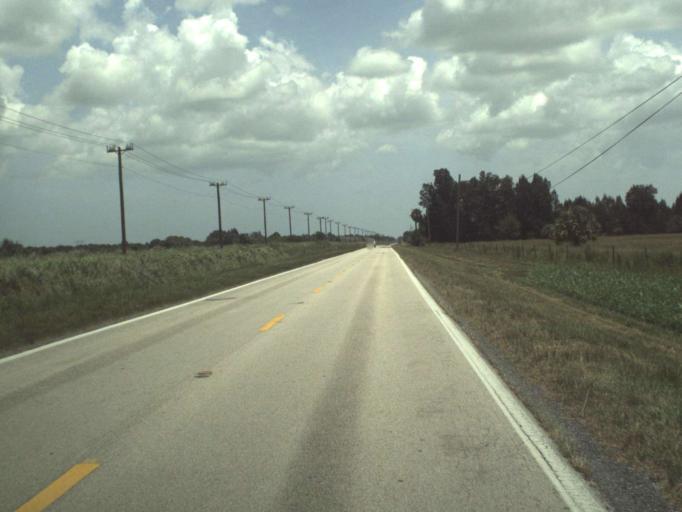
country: US
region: Florida
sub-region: Saint Lucie County
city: Fort Pierce South
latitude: 27.3744
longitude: -80.4679
